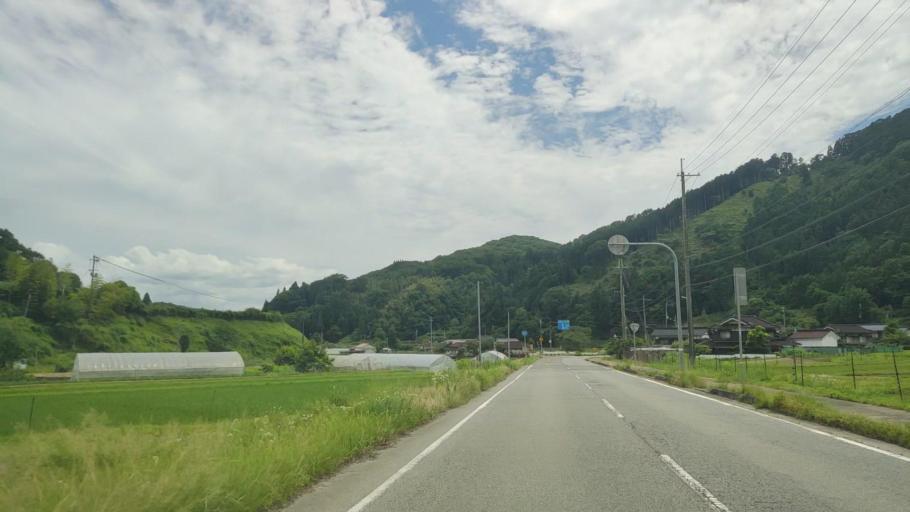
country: JP
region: Hyogo
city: Yamazakicho-nakabirose
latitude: 35.0549
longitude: 134.3660
